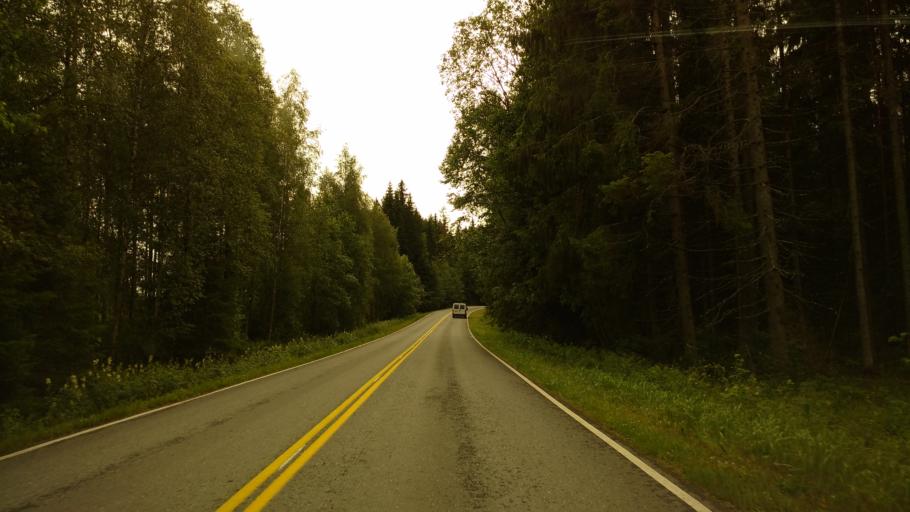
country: FI
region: Varsinais-Suomi
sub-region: Salo
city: Kuusjoki
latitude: 60.5517
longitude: 23.1593
